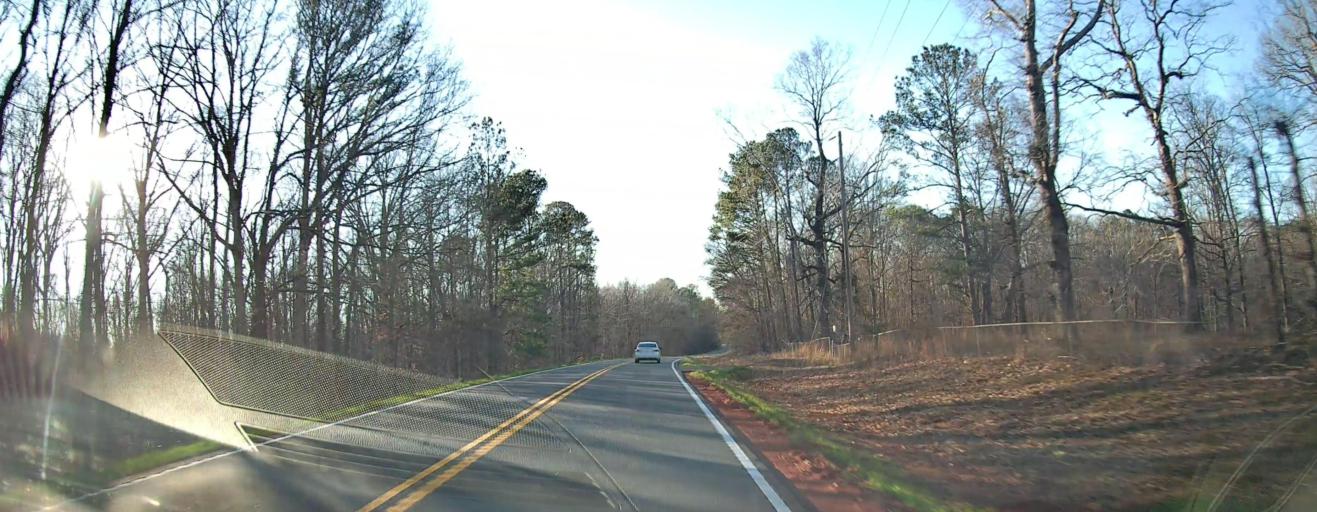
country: US
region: Georgia
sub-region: Meriwether County
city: Greenville
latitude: 32.9128
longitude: -84.7435
